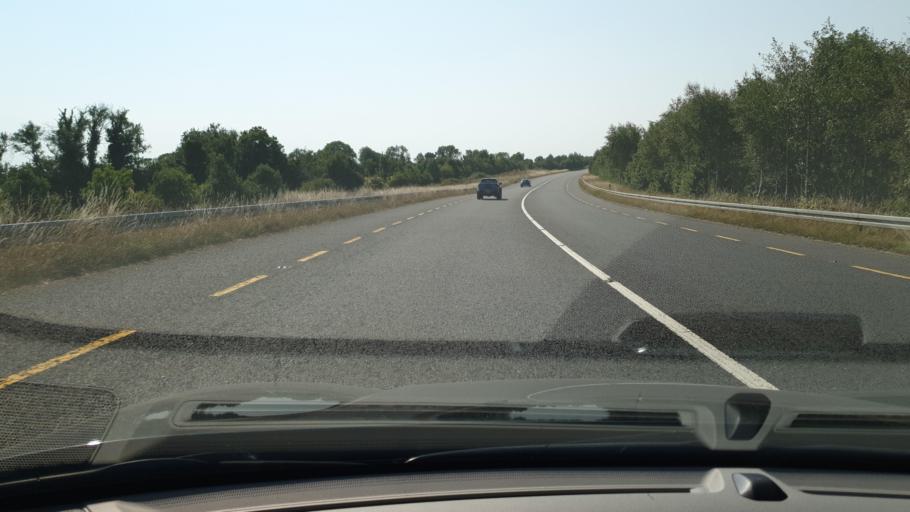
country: IE
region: Leinster
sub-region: An Mhi
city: Dunshaughlin
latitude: 53.5018
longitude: -6.5766
